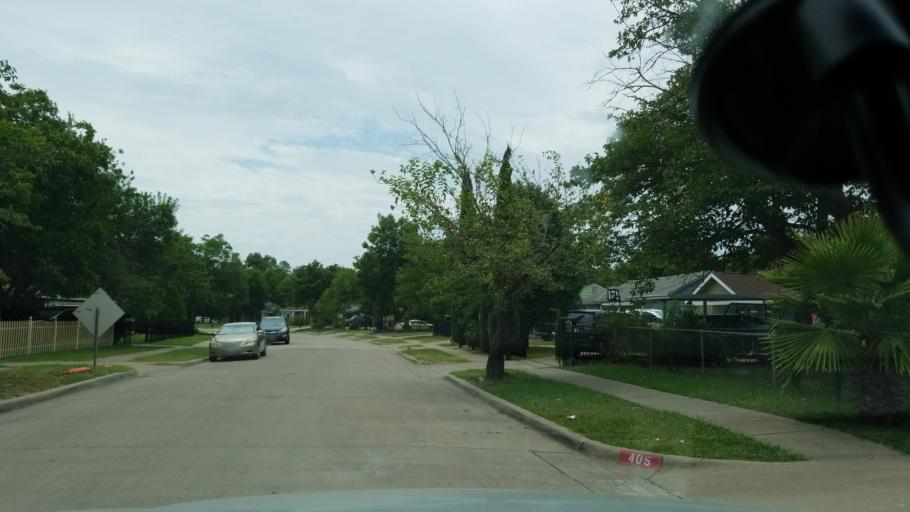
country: US
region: Texas
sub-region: Dallas County
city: Grand Prairie
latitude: 32.7421
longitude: -96.9915
